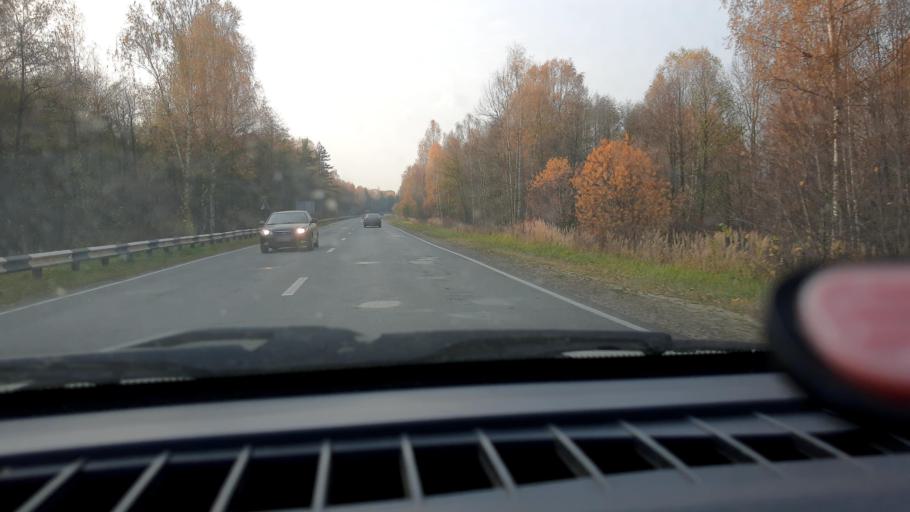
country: RU
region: Nizjnij Novgorod
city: Gorodets
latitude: 56.6147
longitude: 43.5724
